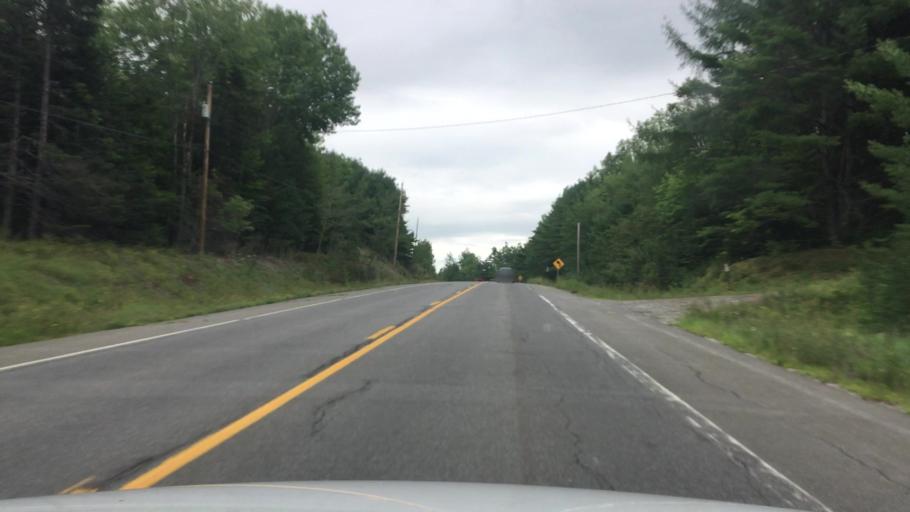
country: US
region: Maine
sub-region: Penobscot County
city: Bradley
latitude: 44.8244
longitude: -68.4035
